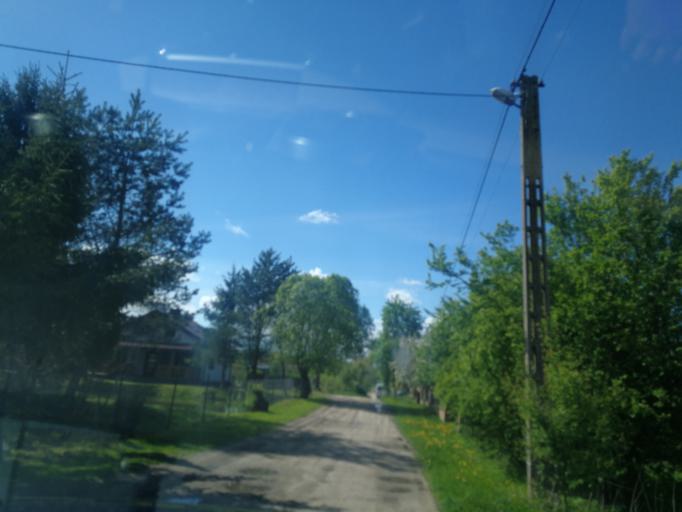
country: PL
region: Warmian-Masurian Voivodeship
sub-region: Powiat ilawski
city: Zalewo
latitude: 53.7624
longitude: 19.6719
